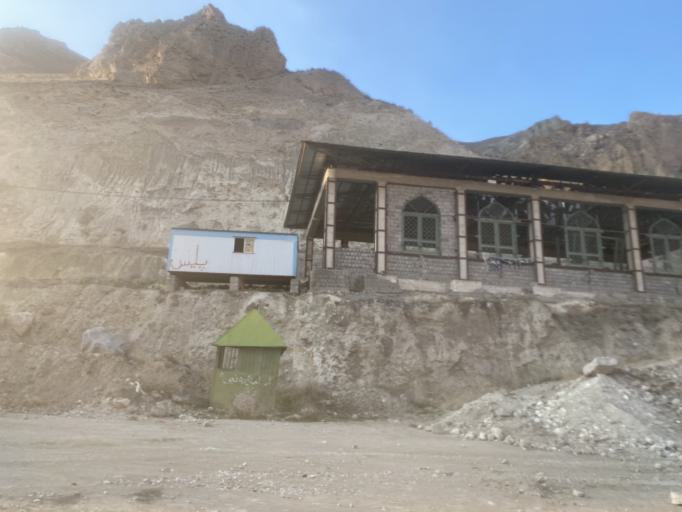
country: IR
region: Tehran
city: Damavand
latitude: 35.9010
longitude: 52.2165
